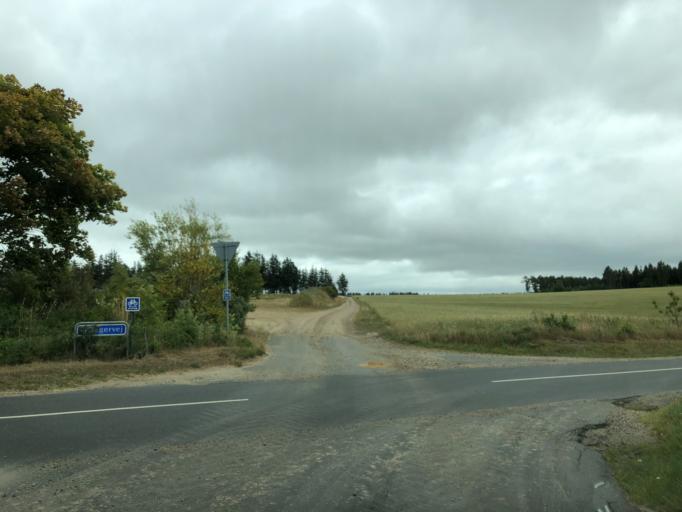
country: DK
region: Central Jutland
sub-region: Herning Kommune
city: Vildbjerg
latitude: 56.2311
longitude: 8.6437
